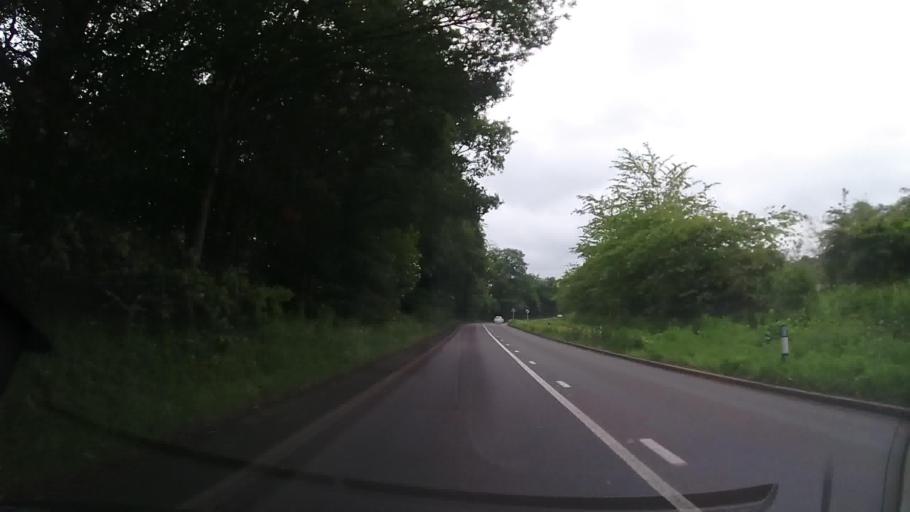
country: GB
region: England
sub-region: Staffordshire
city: Newcastle under Lyme
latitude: 52.9706
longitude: -2.2766
